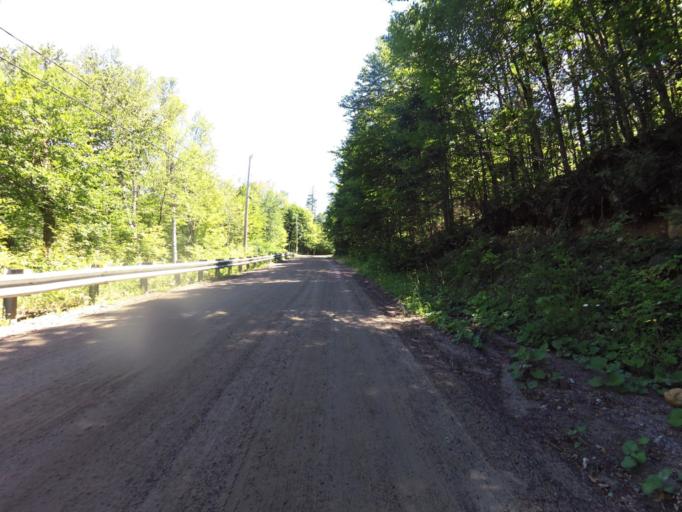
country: CA
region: Quebec
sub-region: Laurentides
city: Brownsburg-Chatham
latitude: 45.8308
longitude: -74.5450
